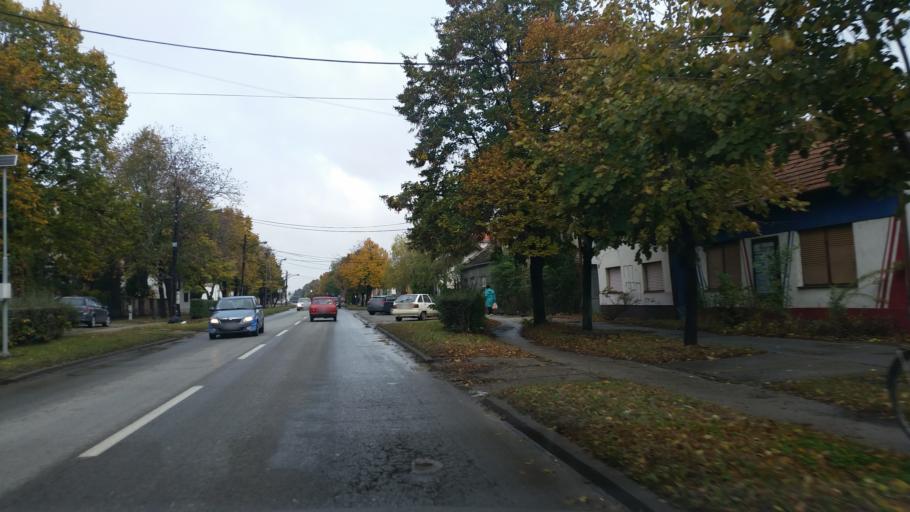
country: RS
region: Autonomna Pokrajina Vojvodina
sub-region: Srednjebanatski Okrug
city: Zrenjanin
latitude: 45.3889
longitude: 20.3802
